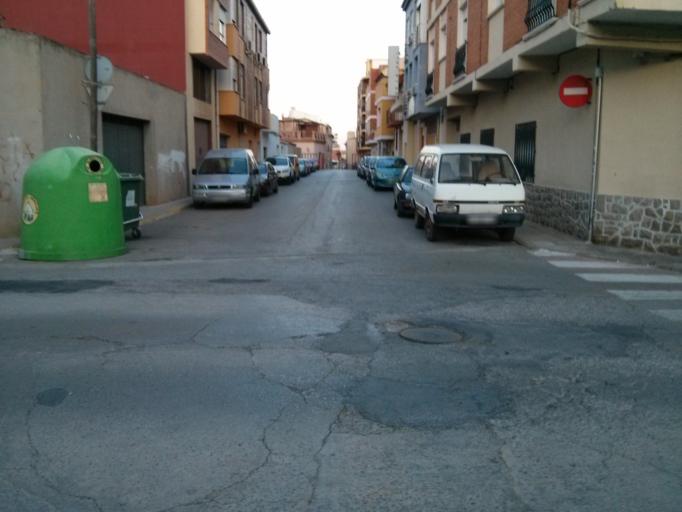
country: ES
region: Valencia
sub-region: Provincia de Castello
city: Alfondeguilla
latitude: 39.8239
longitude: -0.2268
